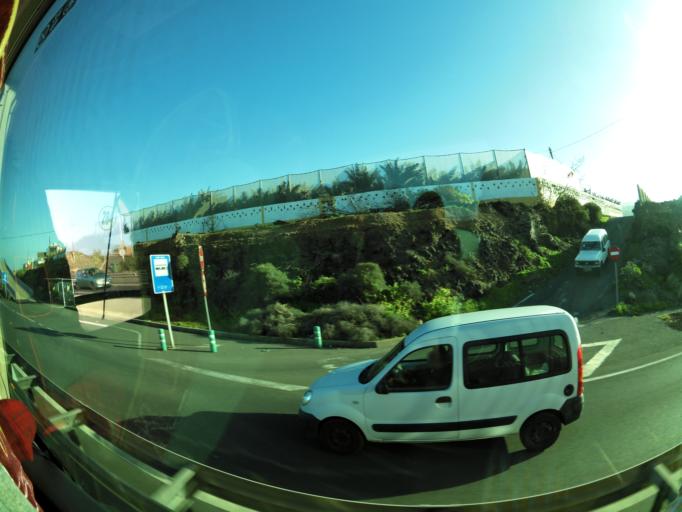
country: ES
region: Canary Islands
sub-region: Provincia de Las Palmas
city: Arucas
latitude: 28.1520
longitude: -15.5272
